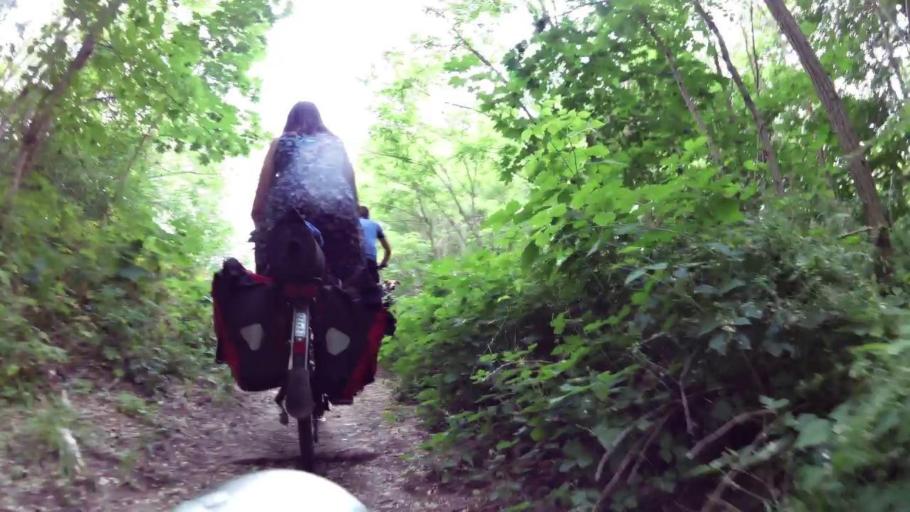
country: PL
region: Kujawsko-Pomorskie
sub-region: Bydgoszcz
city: Fordon
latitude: 53.1437
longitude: 18.1606
